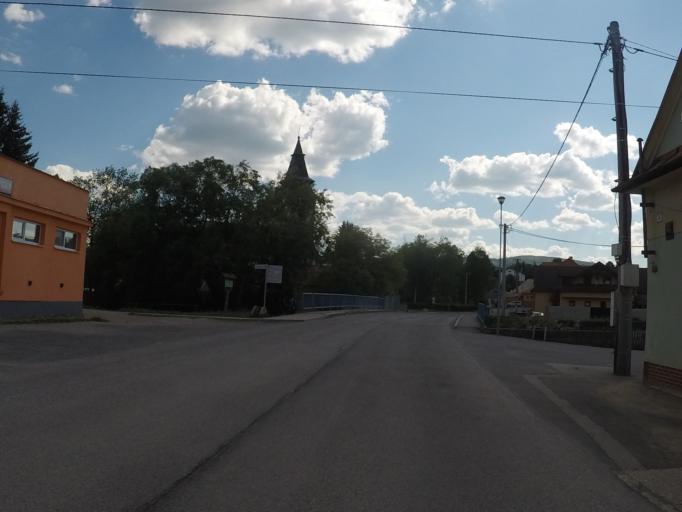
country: SK
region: Presovsky
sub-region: Okres Poprad
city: Poprad
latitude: 48.9957
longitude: 20.3593
